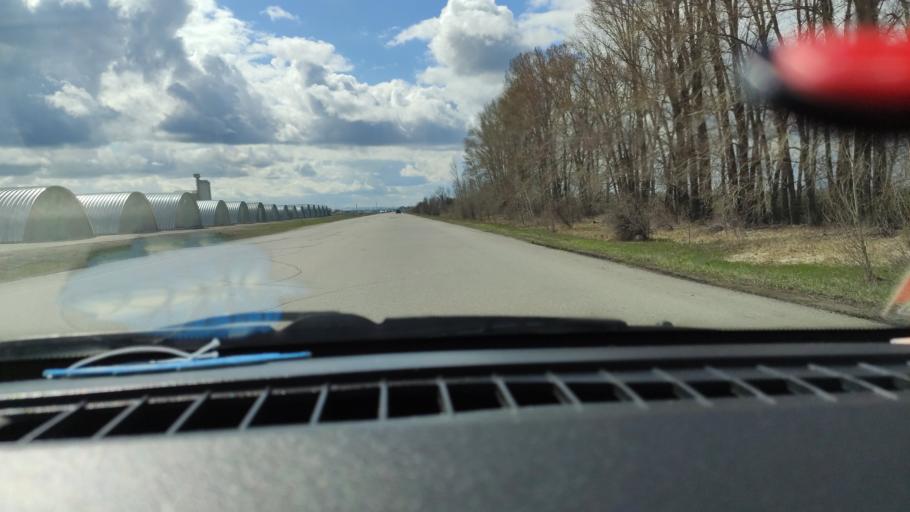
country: RU
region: Samara
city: Tol'yatti
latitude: 53.6861
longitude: 49.4171
